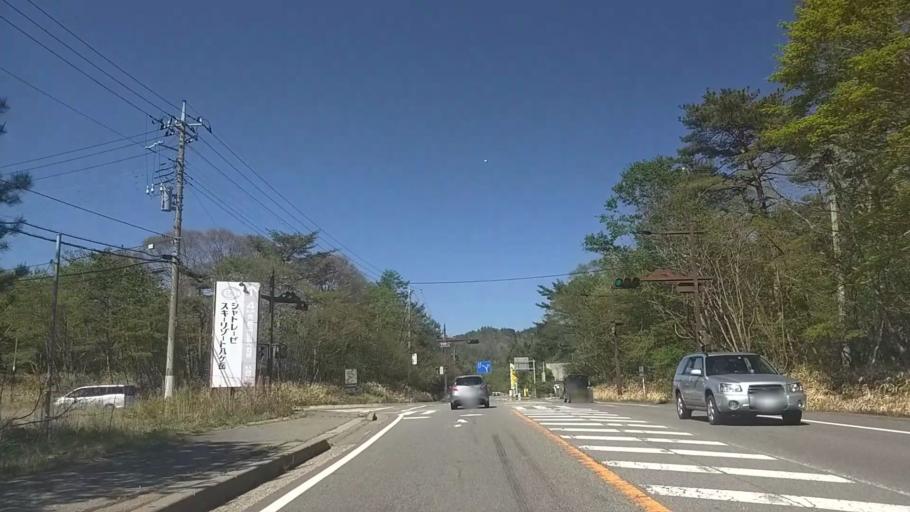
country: JP
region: Yamanashi
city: Nirasaki
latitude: 35.9306
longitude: 138.4448
